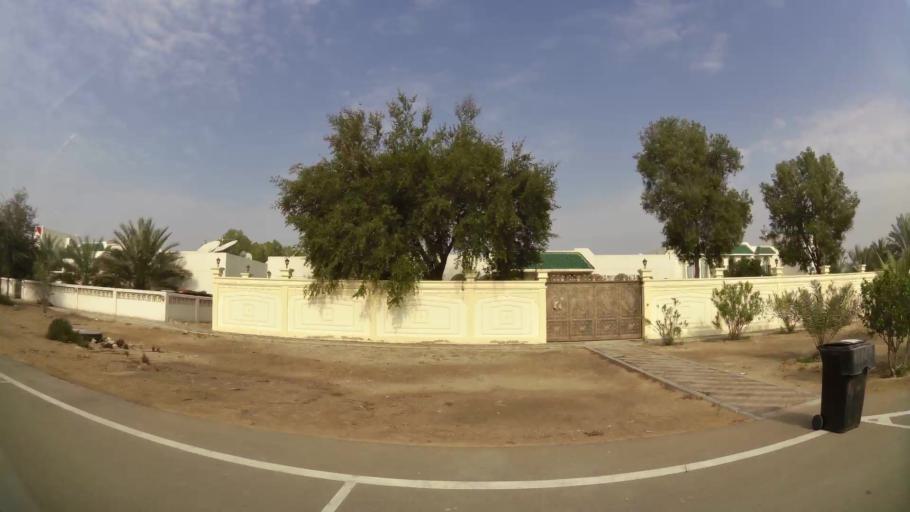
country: AE
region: Abu Dhabi
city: Abu Dhabi
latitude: 24.6624
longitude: 54.7612
